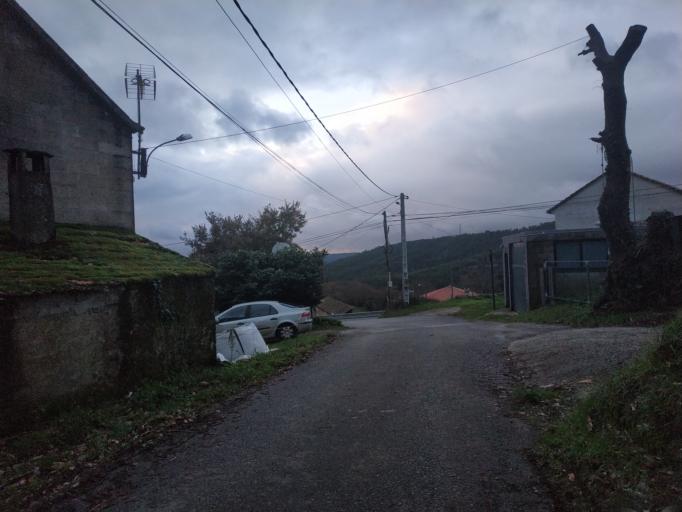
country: ES
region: Galicia
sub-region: Provincia de Pontevedra
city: Silleda
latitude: 42.7837
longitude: -8.1696
